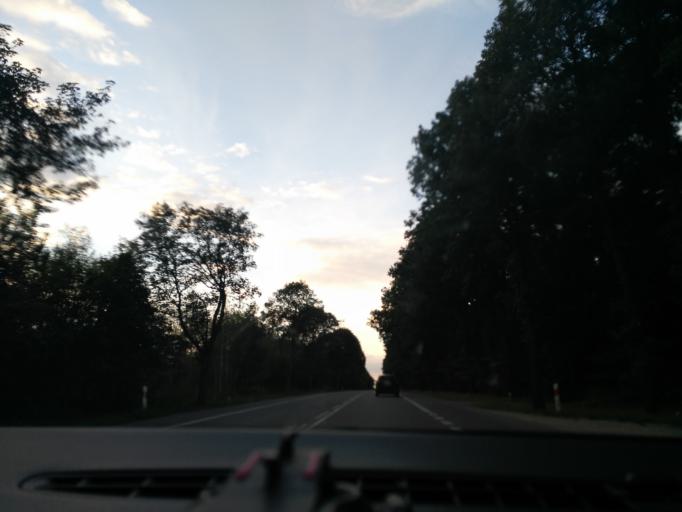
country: PL
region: Lublin Voivodeship
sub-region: Powiat lubelski
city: Niemce
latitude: 51.3930
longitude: 22.6363
